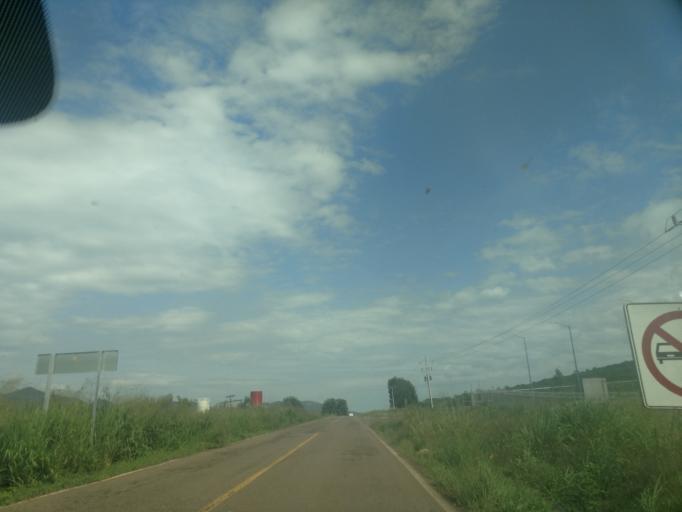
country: MX
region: Jalisco
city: Talpa de Allende
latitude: 20.4396
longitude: -104.7505
